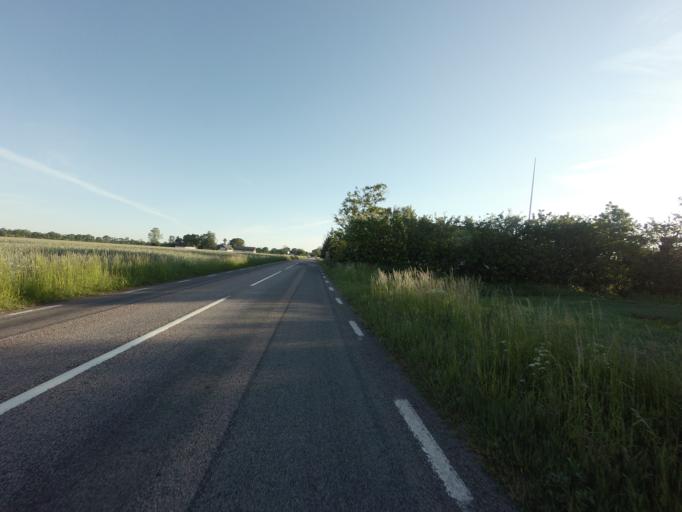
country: SE
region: Skane
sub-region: Helsingborg
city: Odakra
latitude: 56.1997
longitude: 12.6745
